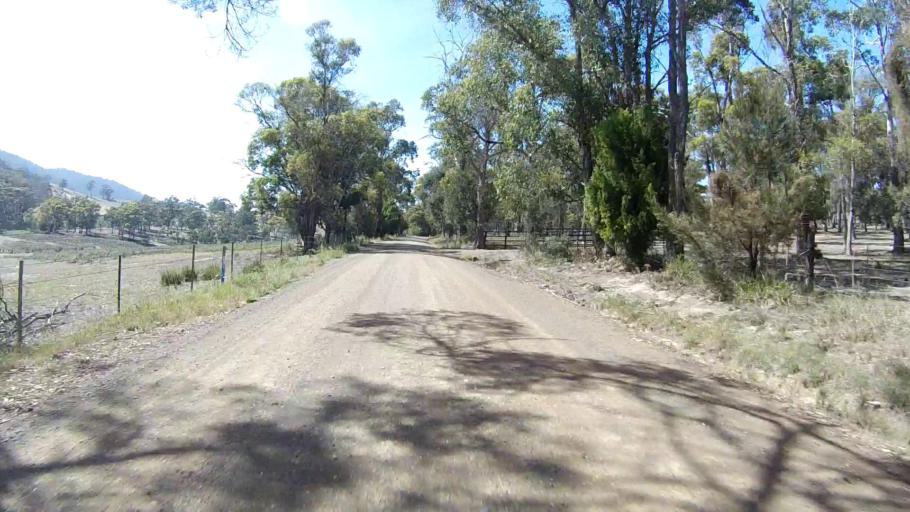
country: AU
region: Tasmania
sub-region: Sorell
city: Sorell
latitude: -42.7360
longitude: 147.5962
